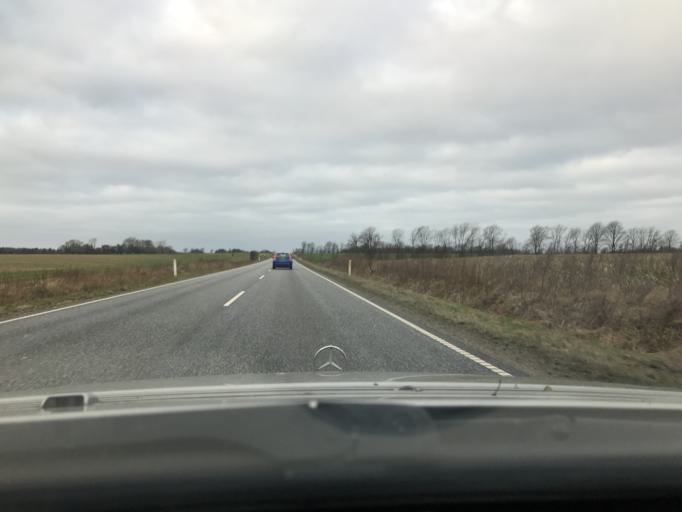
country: DK
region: South Denmark
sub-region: Tonder Kommune
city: Toftlund
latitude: 55.1111
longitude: 9.1742
